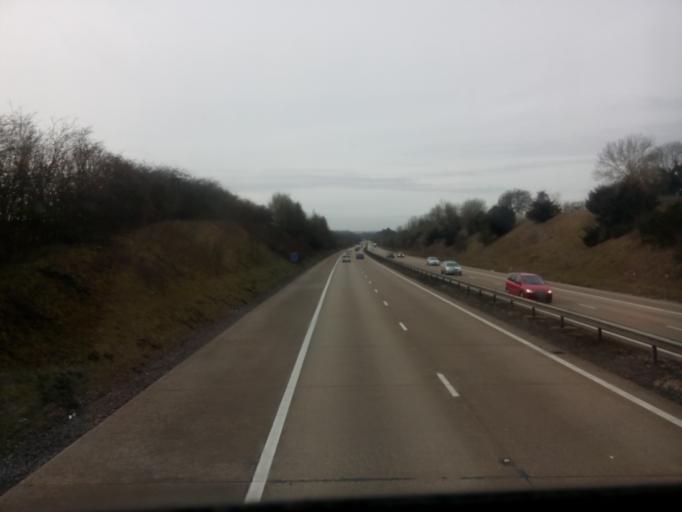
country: GB
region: England
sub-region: Hampshire
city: Overton
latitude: 51.1862
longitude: -1.2109
